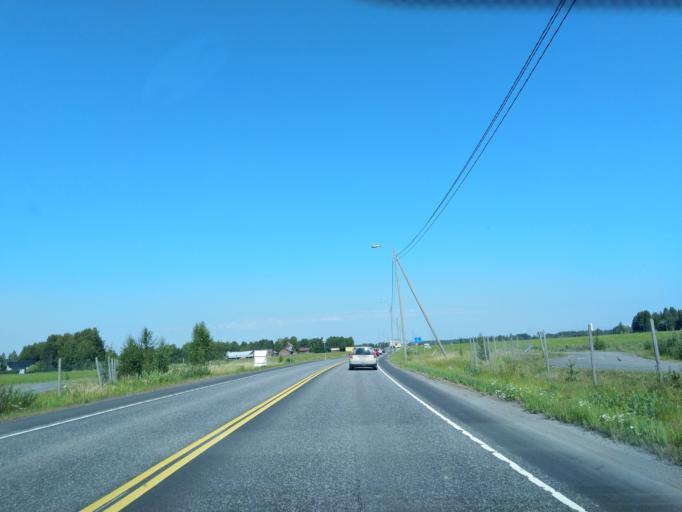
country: FI
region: Satakunta
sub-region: Pori
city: Nakkila
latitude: 61.3467
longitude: 22.0202
